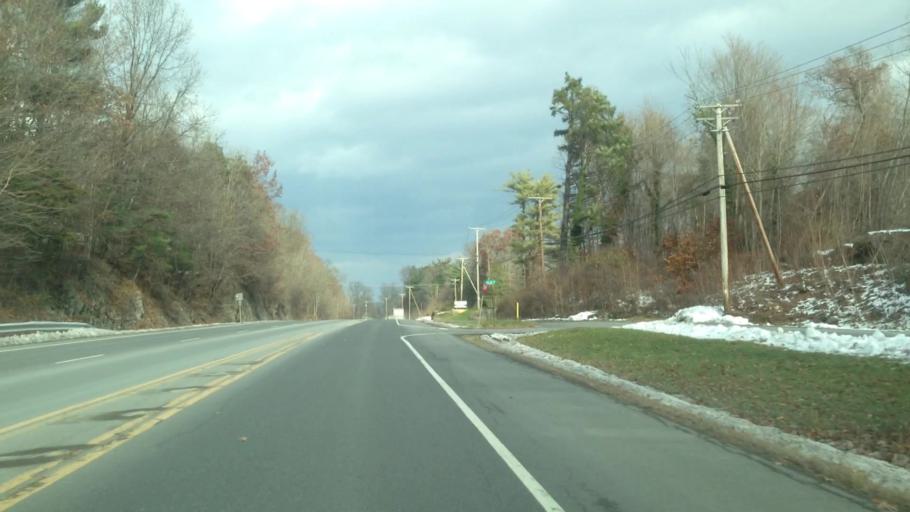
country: US
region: New York
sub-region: Ulster County
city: Lincoln Park
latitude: 41.9542
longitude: -73.9756
